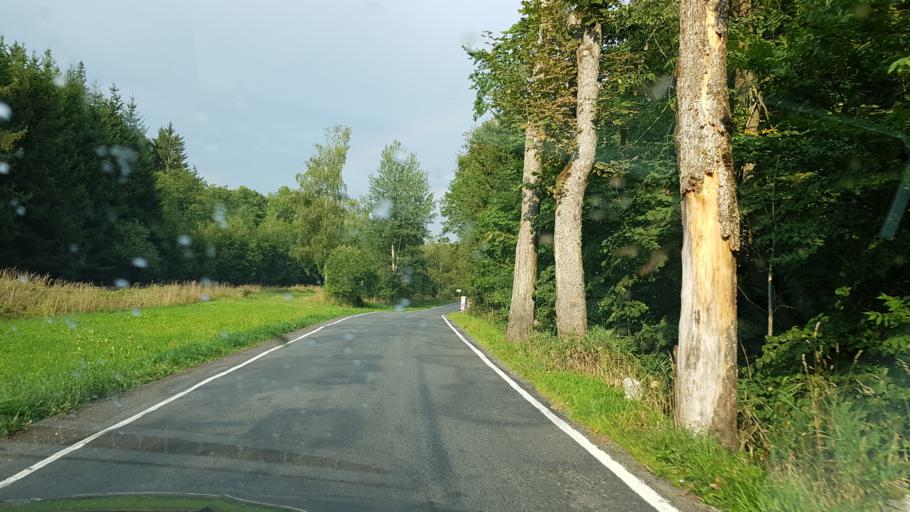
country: CZ
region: Pardubicky
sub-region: Okres Usti nad Orlici
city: Kraliky
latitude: 50.0861
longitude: 16.8399
